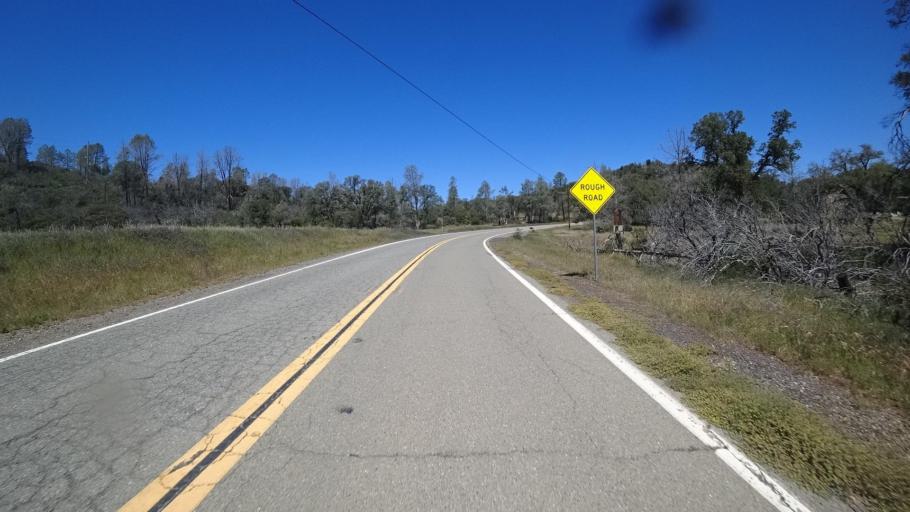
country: US
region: California
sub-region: Lake County
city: Hidden Valley Lake
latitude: 38.8876
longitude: -122.4801
